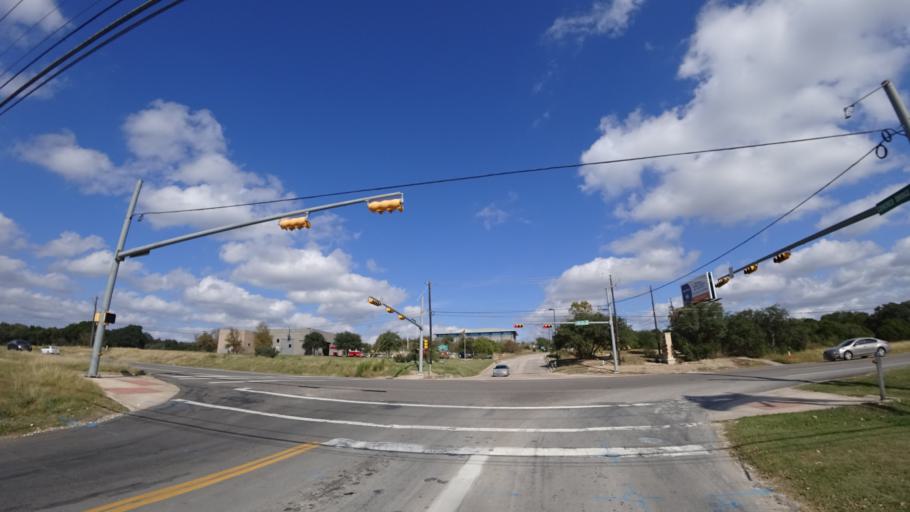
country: US
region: Texas
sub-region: Travis County
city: Barton Creek
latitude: 30.2497
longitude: -97.8944
